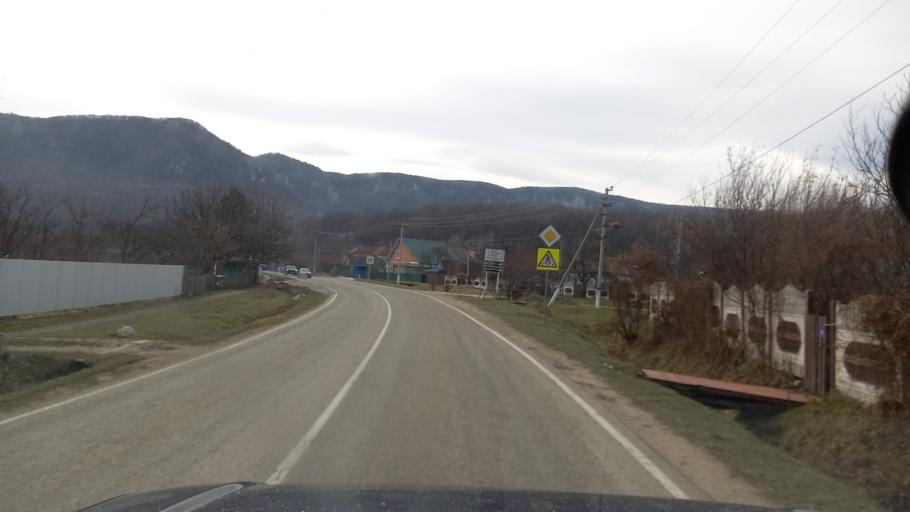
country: RU
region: Krasnodarskiy
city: Neftegorsk
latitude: 44.2357
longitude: 39.9033
